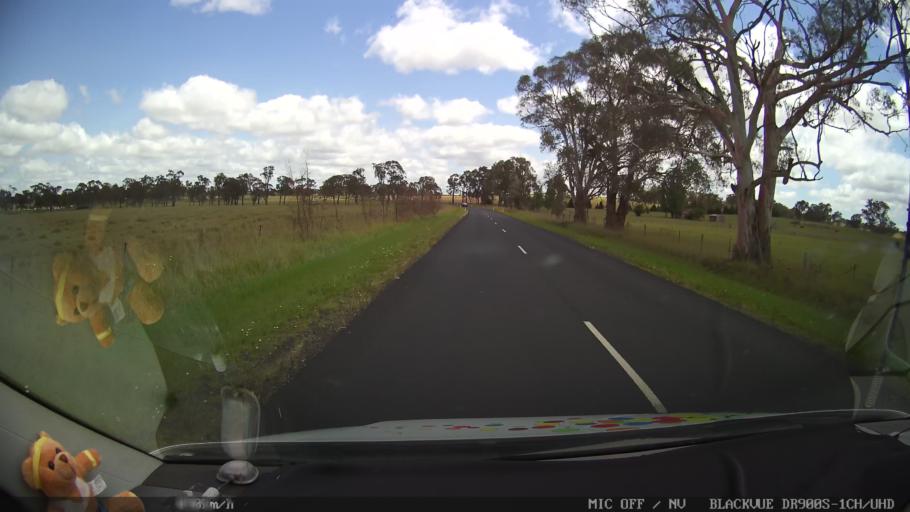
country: AU
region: New South Wales
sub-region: Glen Innes Severn
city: Glen Innes
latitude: -29.6537
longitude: 151.6934
